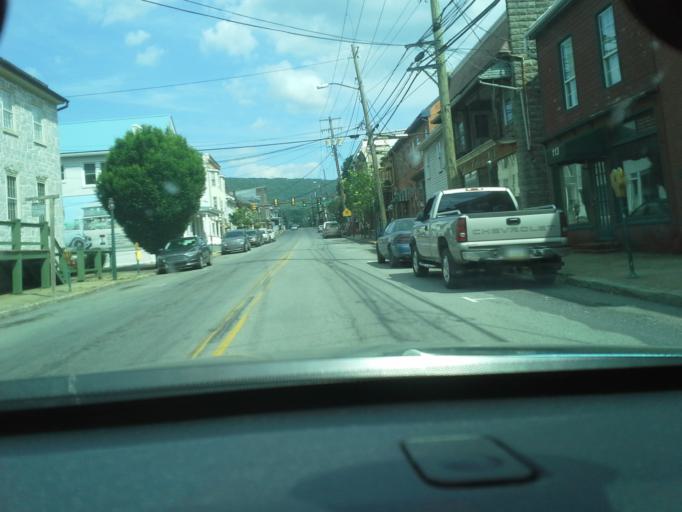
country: US
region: Pennsylvania
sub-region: Fulton County
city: McConnellsburg
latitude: 39.9324
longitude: -77.9987
